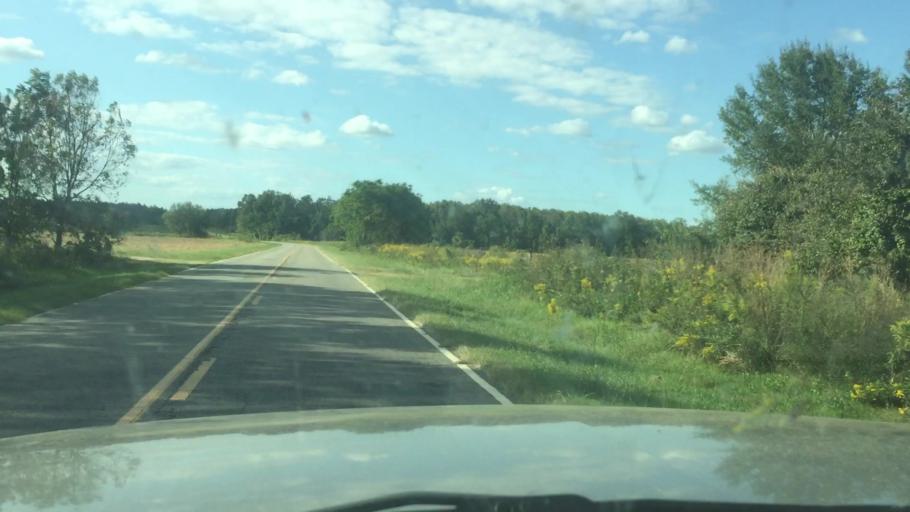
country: US
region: Georgia
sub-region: Terrell County
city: Dawson
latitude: 31.7371
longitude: -84.3439
